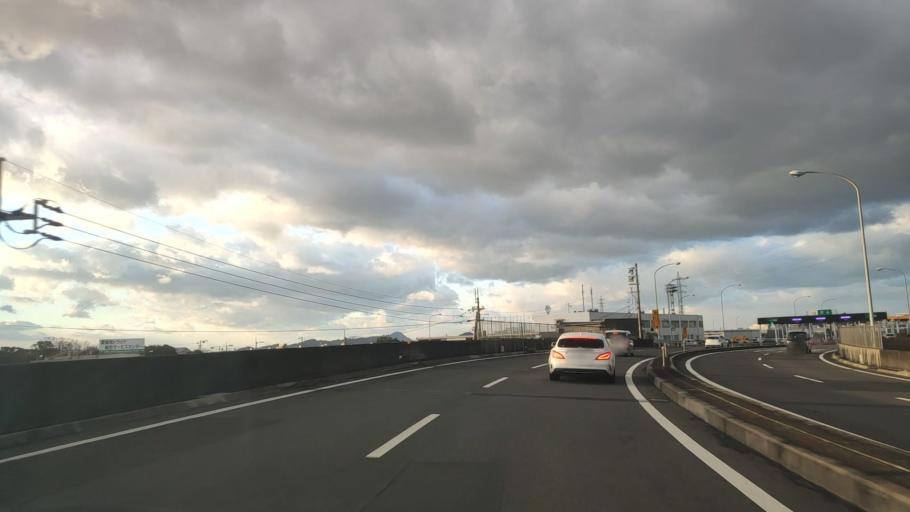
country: JP
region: Ehime
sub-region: Shikoku-chuo Shi
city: Matsuyama
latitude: 33.7969
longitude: 132.7785
